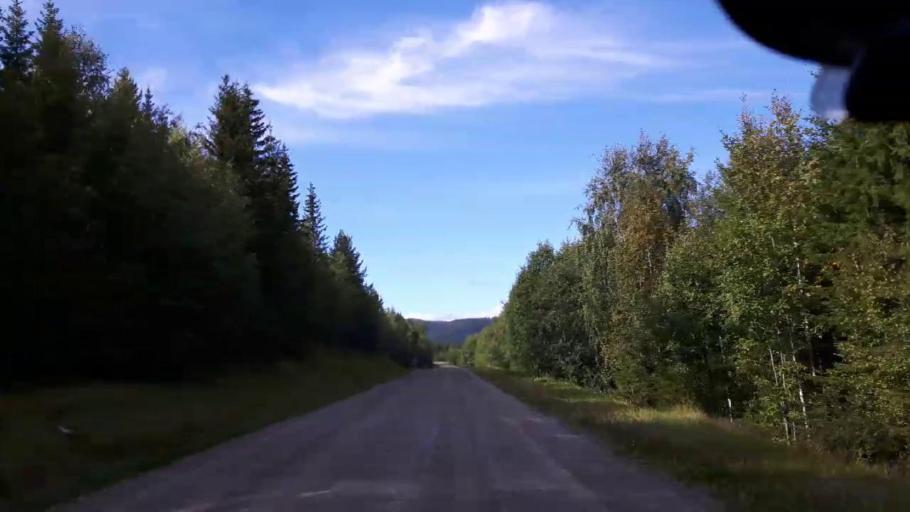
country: SE
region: Jaemtland
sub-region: Ragunda Kommun
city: Hammarstrand
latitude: 63.1336
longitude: 16.1159
